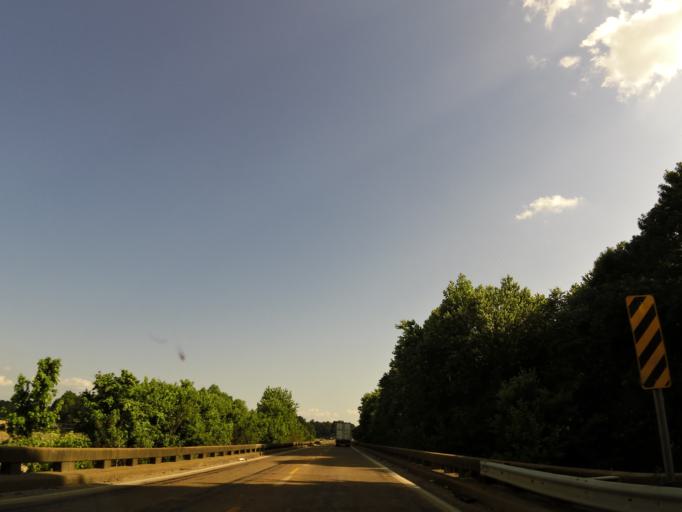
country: US
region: Mississippi
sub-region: Lafayette County
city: University
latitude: 34.2696
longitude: -89.5219
